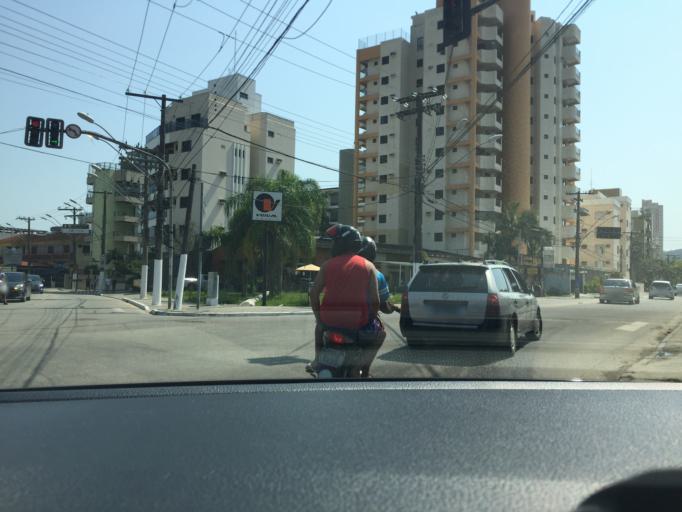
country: BR
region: Sao Paulo
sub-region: Guaruja
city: Guaruja
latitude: -23.9846
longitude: -46.2020
